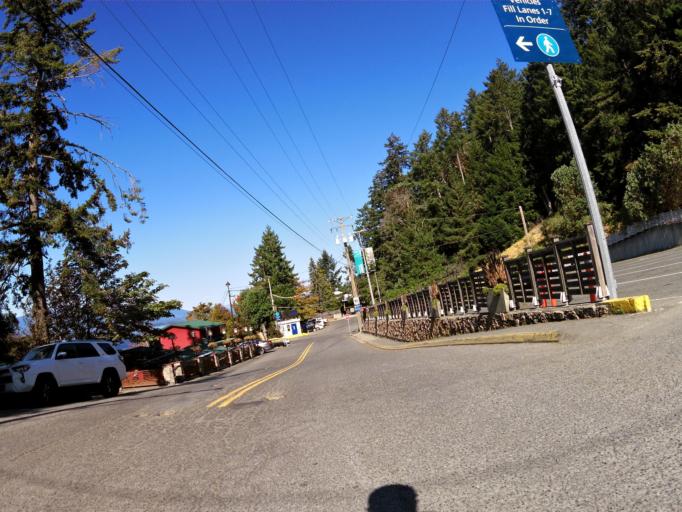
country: CA
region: British Columbia
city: North Cowichan
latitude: 48.8815
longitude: -123.5716
